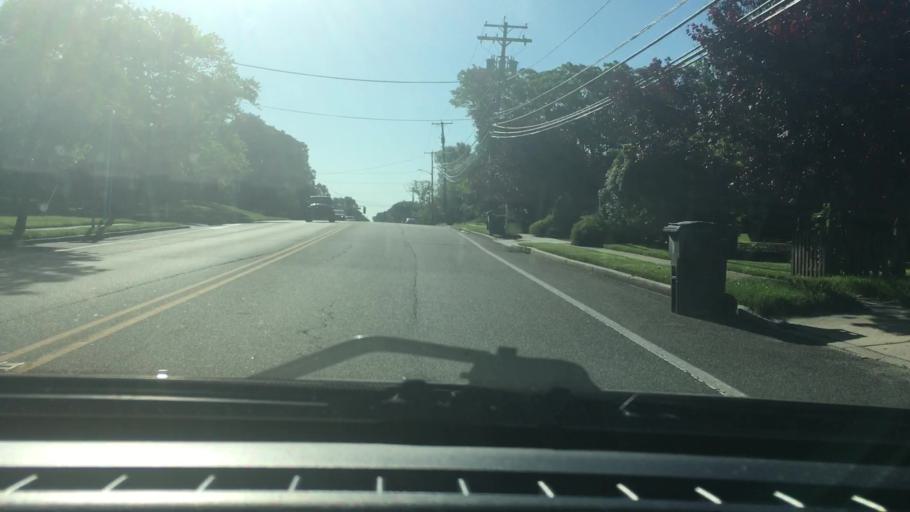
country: US
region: New Jersey
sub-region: Ocean County
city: Island Heights
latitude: 39.9703
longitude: -74.1531
